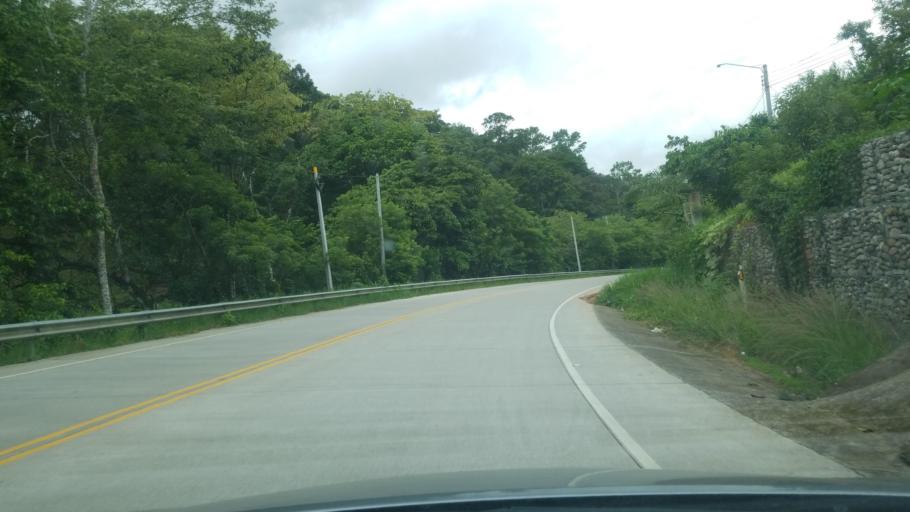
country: HN
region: Copan
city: San Jeronimo
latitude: 14.9473
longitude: -88.9106
